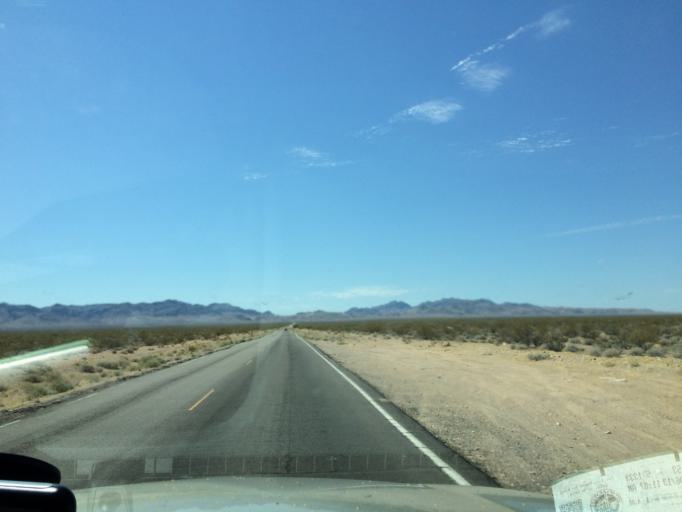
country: US
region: Nevada
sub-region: Clark County
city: Moapa Town
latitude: 36.4728
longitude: -114.7422
